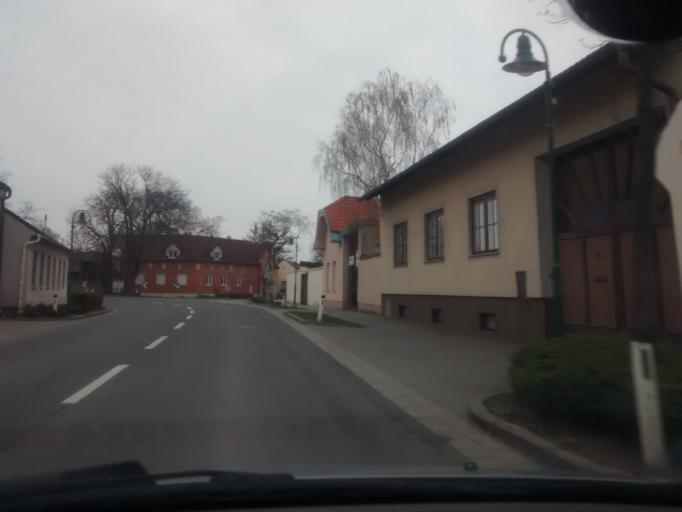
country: AT
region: Lower Austria
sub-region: Politischer Bezirk Modling
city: Munchendorf
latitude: 48.0320
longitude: 16.3811
